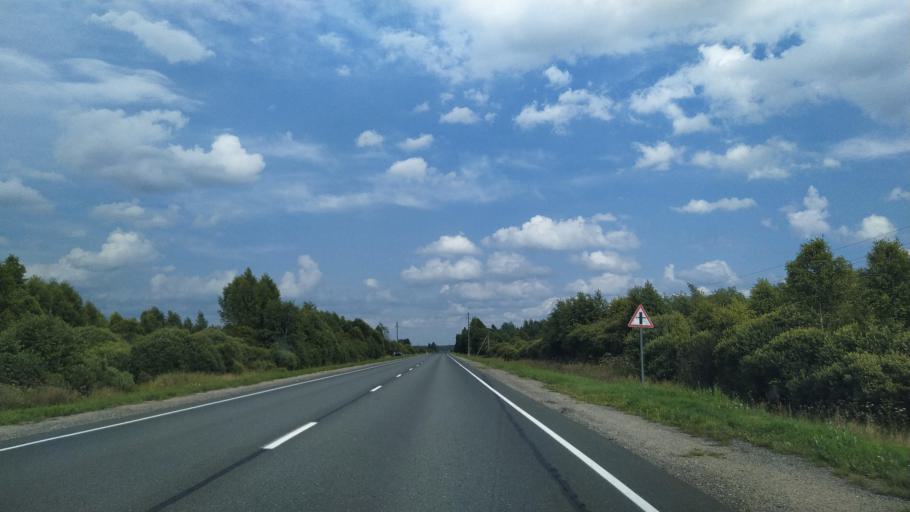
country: RU
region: Pskov
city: Porkhov
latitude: 57.9787
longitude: 29.7220
